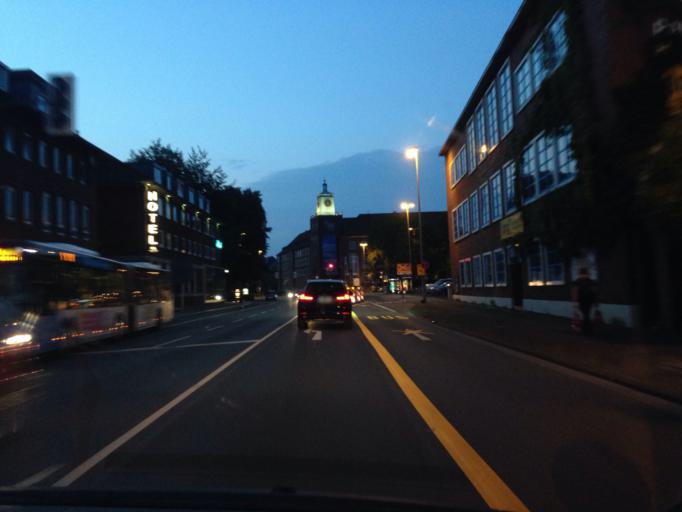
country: DE
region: North Rhine-Westphalia
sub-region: Regierungsbezirk Munster
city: Muenster
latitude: 51.9607
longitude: 7.6352
